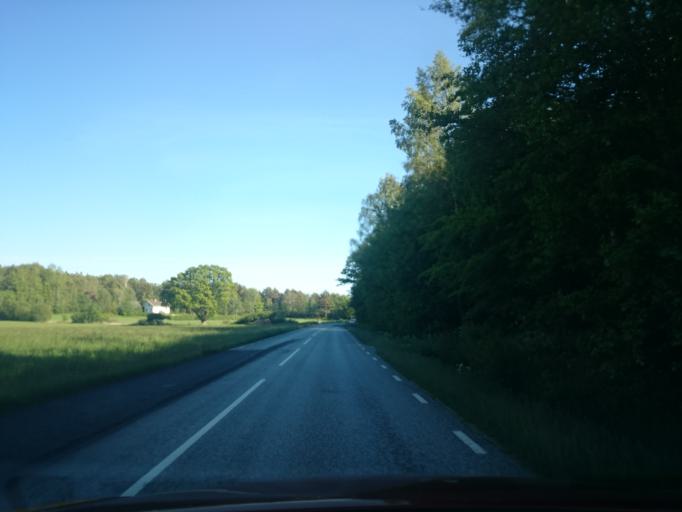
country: SE
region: Vaestra Goetaland
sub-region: Lysekils Kommun
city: Lysekil
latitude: 58.2671
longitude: 11.5372
